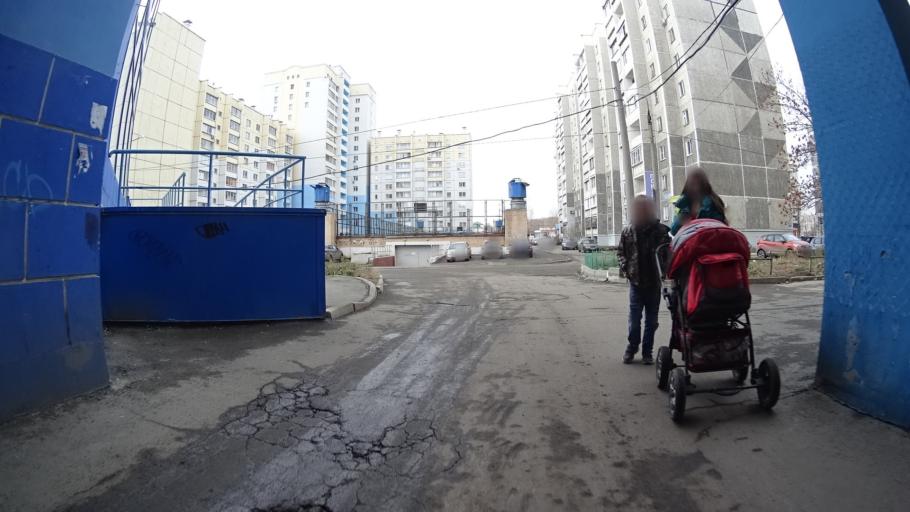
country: RU
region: Chelyabinsk
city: Roshchino
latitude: 55.1845
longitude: 61.2935
